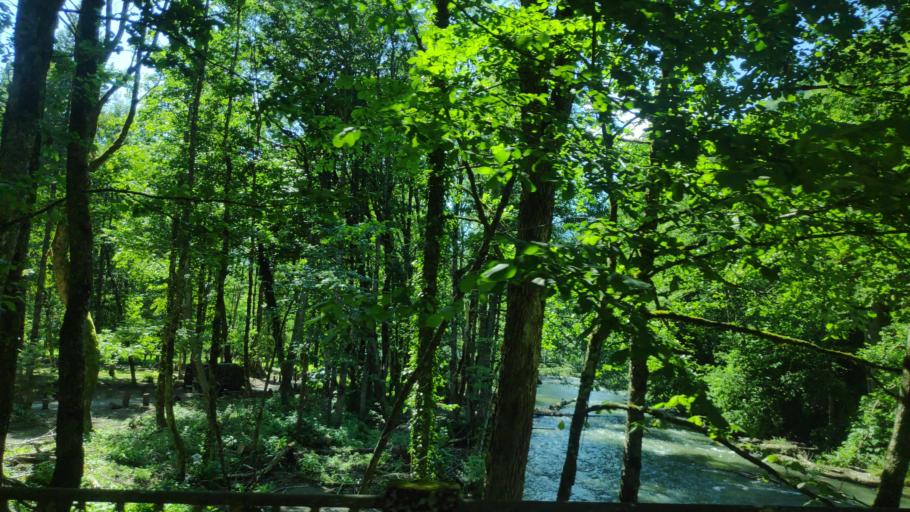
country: GE
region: Abkhazia
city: Gagra
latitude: 43.4815
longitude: 40.5628
